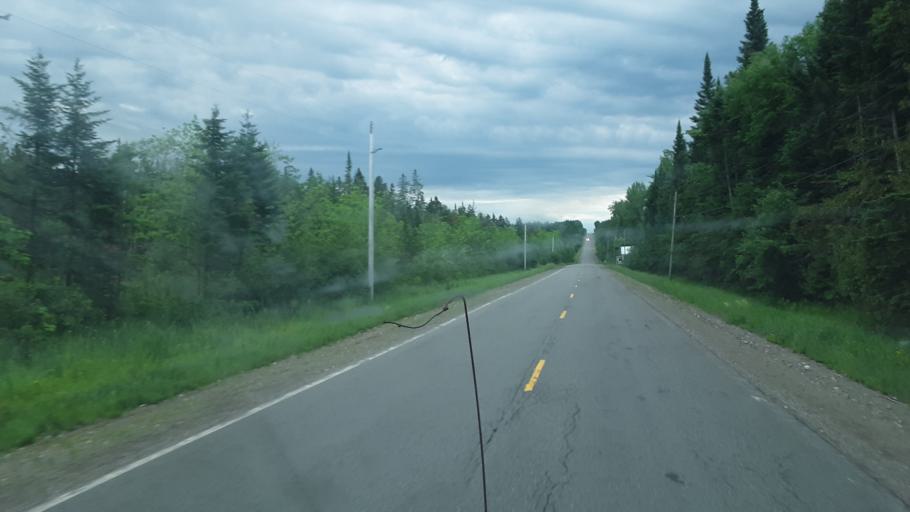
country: US
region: Maine
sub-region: Penobscot County
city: Patten
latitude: 45.8316
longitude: -68.3247
